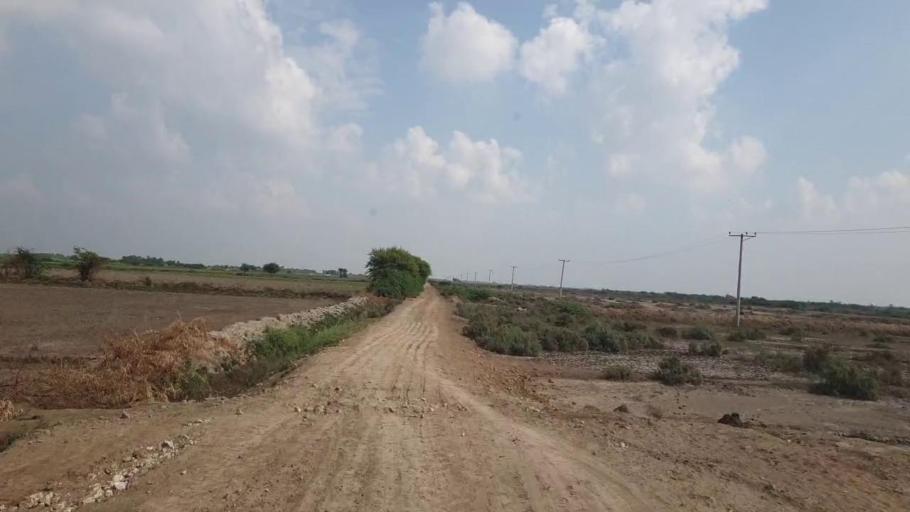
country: PK
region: Sindh
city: Badin
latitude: 24.5328
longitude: 68.6211
